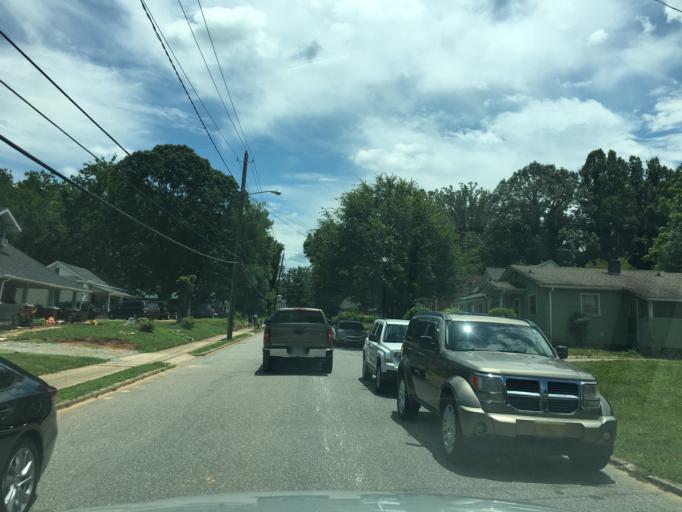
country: US
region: North Carolina
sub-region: Burke County
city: Morganton
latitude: 35.7501
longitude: -81.6935
